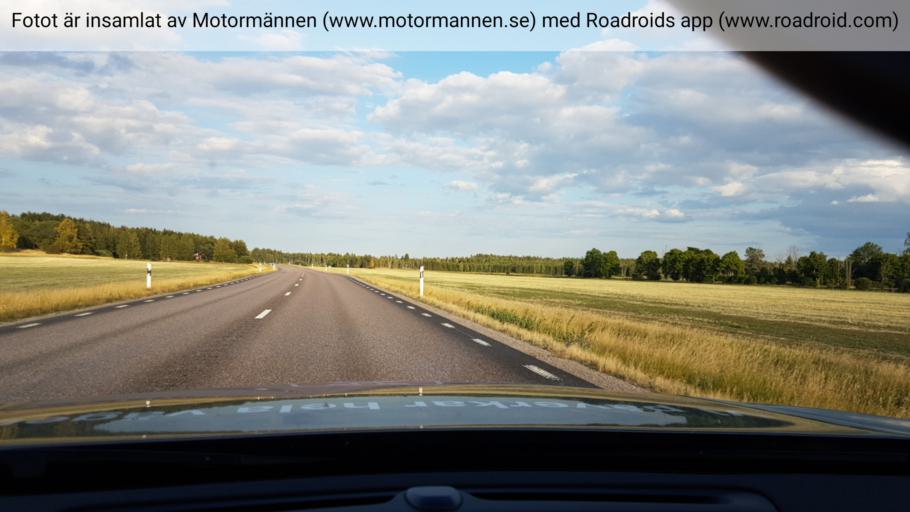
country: SE
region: Uppsala
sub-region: Enkopings Kommun
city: Orsundsbro
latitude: 59.8729
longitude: 17.2981
